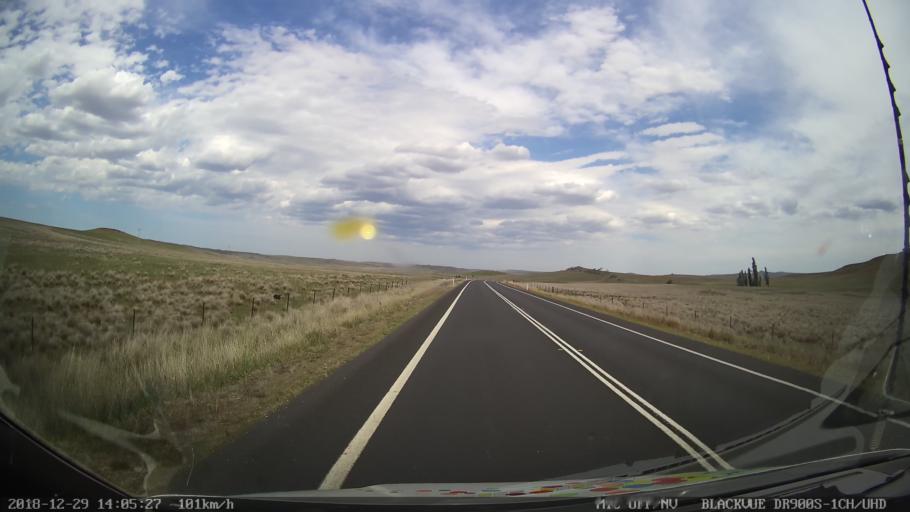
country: AU
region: New South Wales
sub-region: Cooma-Monaro
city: Cooma
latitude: -36.3306
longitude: 149.1917
